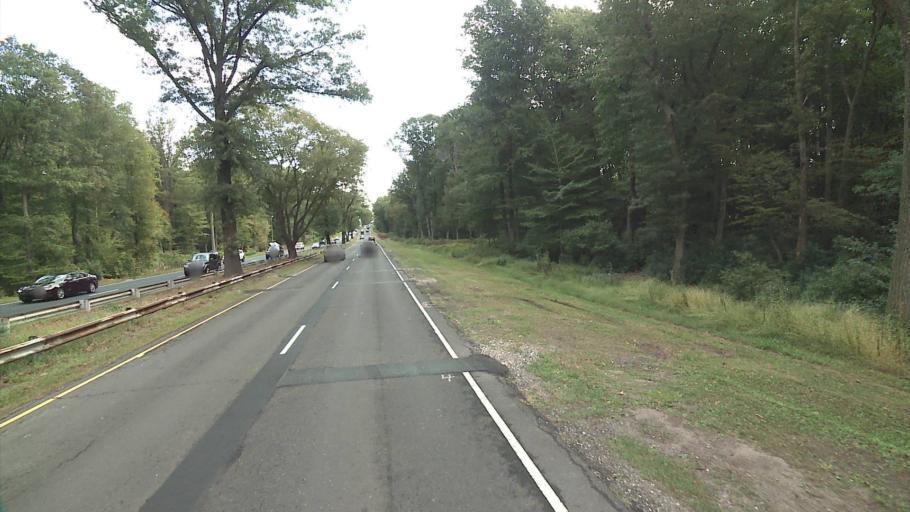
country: US
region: Connecticut
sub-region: Fairfield County
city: Westport
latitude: 41.1704
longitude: -73.3348
